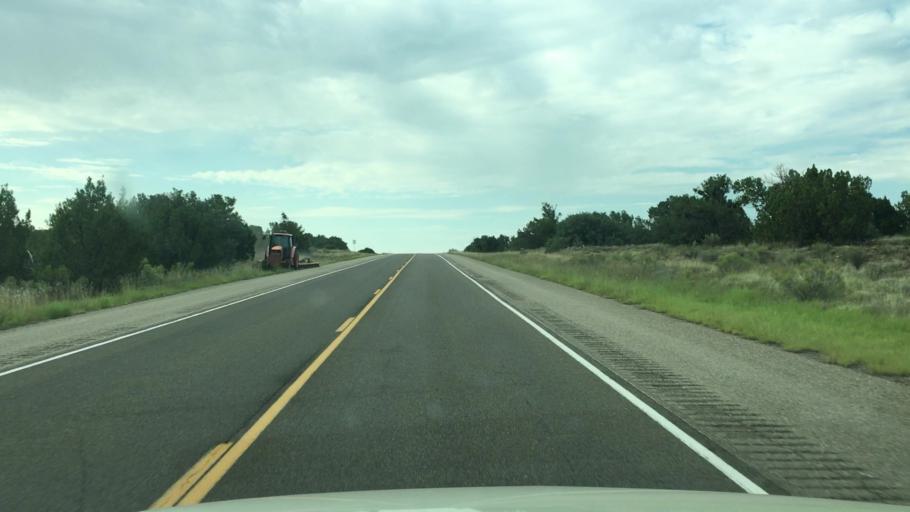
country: US
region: New Mexico
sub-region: Santa Fe County
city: Eldorado at Santa Fe
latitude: 35.2270
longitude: -105.8023
